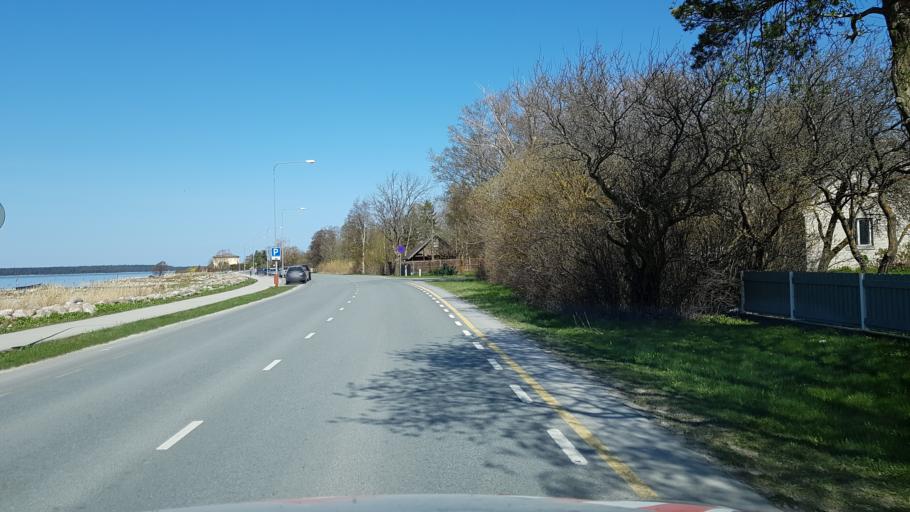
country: EE
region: Harju
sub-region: Viimsi vald
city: Rummu
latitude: 59.5518
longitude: 24.7952
